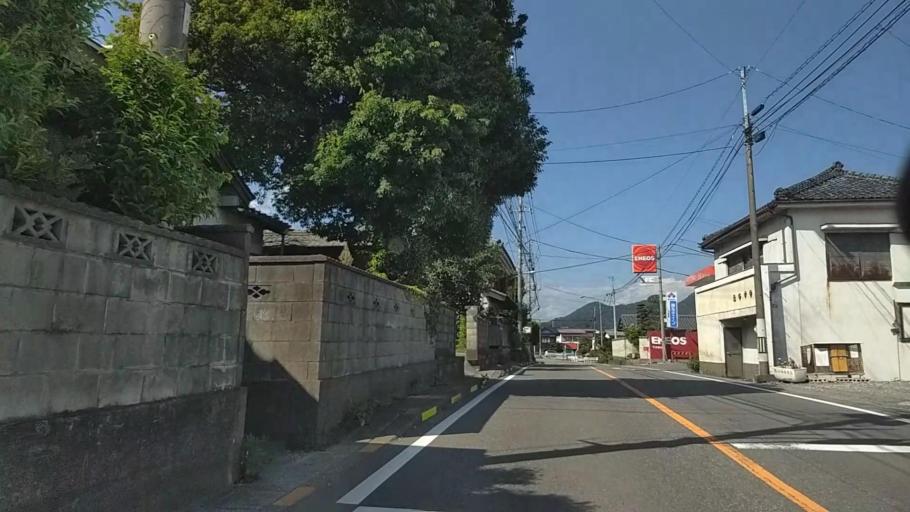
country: JP
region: Yamanashi
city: Ryuo
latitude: 35.4082
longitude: 138.4421
